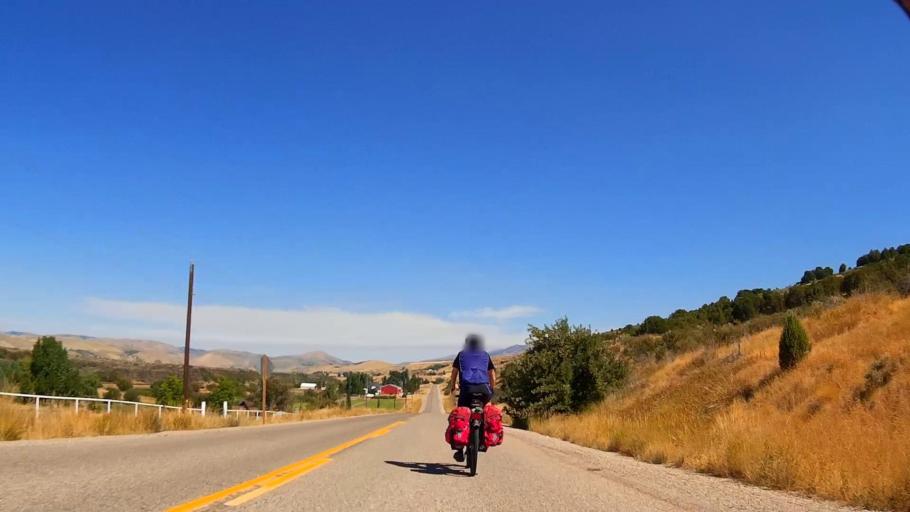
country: US
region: Idaho
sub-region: Bannock County
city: Pocatello
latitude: 42.7116
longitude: -112.2071
